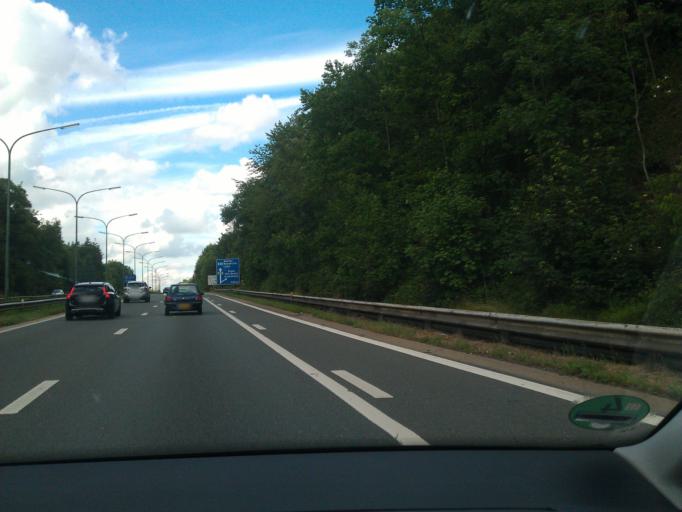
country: BE
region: Wallonia
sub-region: Province de Liege
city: Dison
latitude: 50.5991
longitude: 5.8470
